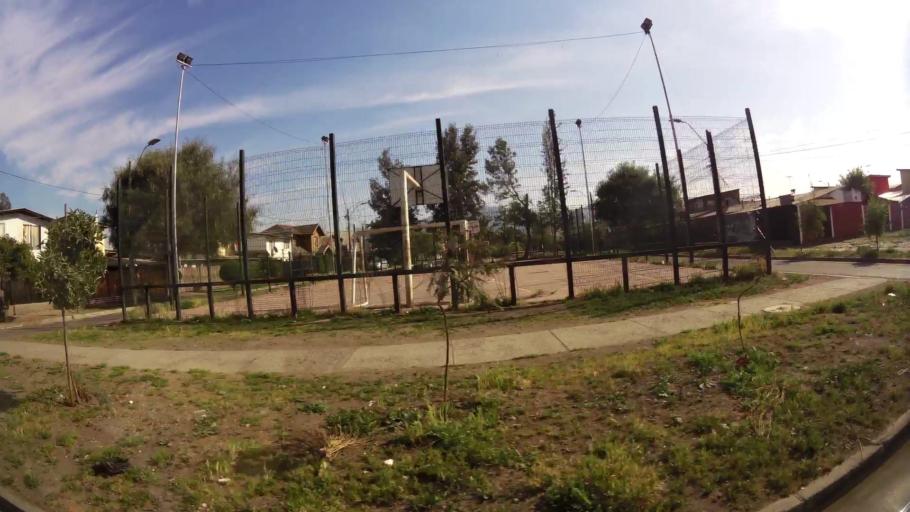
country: CL
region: Santiago Metropolitan
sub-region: Provincia de Talagante
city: Talagante
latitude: -33.6812
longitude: -70.9503
